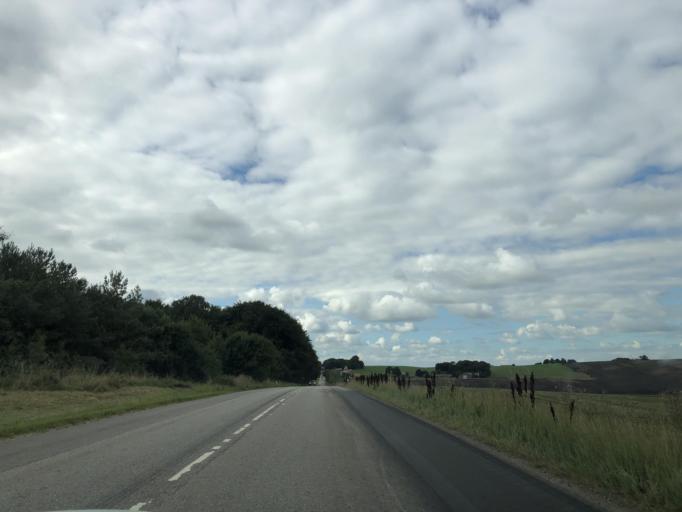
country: DK
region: North Denmark
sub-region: Rebild Kommune
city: Stovring
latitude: 56.8772
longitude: 9.7546
